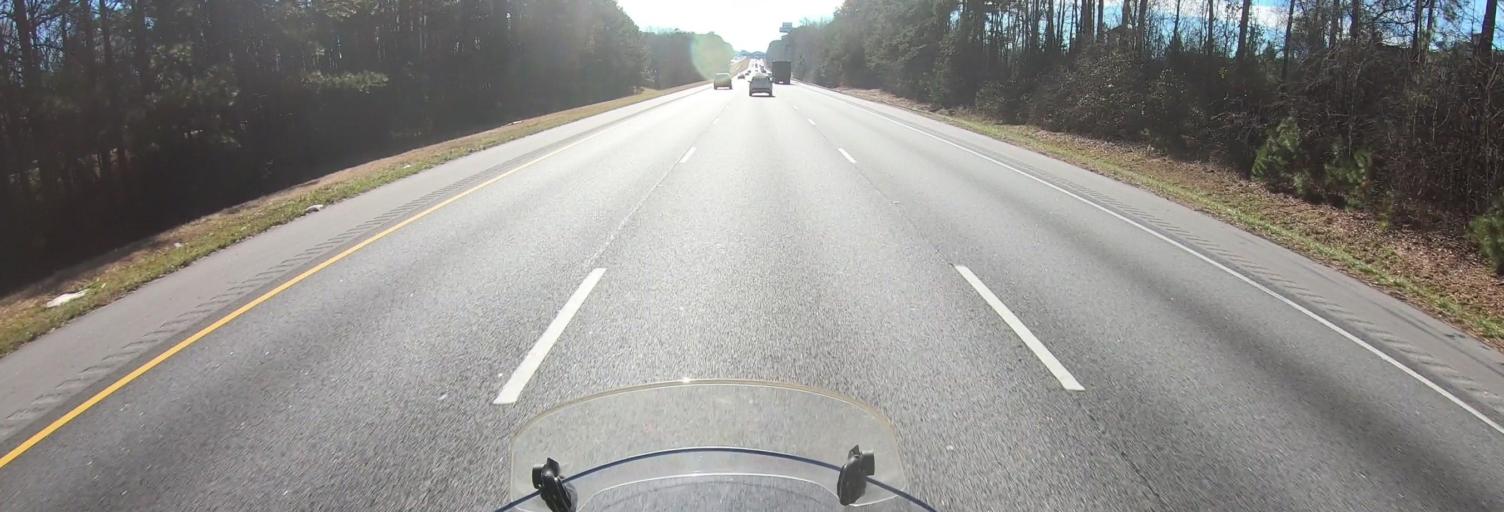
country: US
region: Georgia
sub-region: Henry County
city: Locust Grove
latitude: 33.3866
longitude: -84.1473
